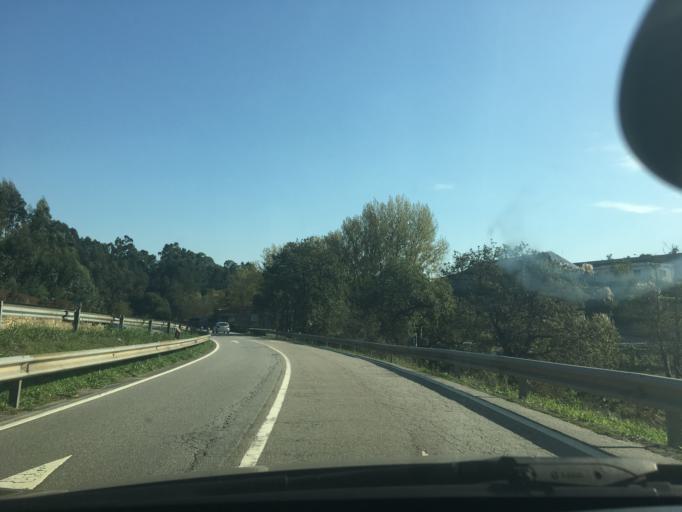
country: PT
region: Porto
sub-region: Maia
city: Maia
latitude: 41.2252
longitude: -8.6327
